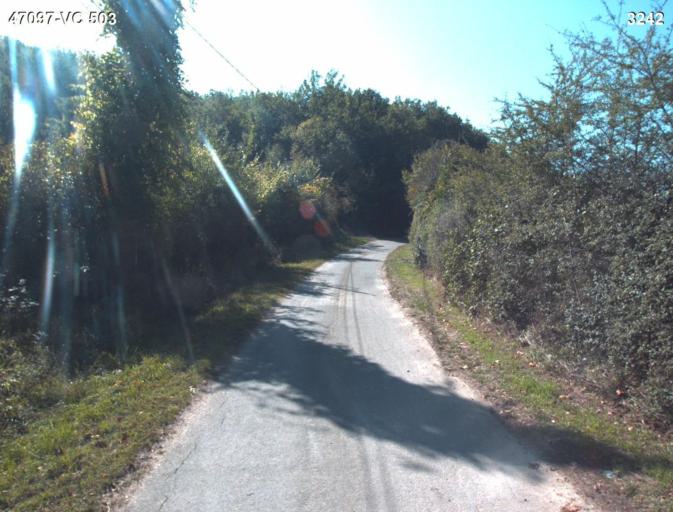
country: FR
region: Aquitaine
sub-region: Departement du Lot-et-Garonne
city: Port-Sainte-Marie
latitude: 44.2170
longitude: 0.3745
